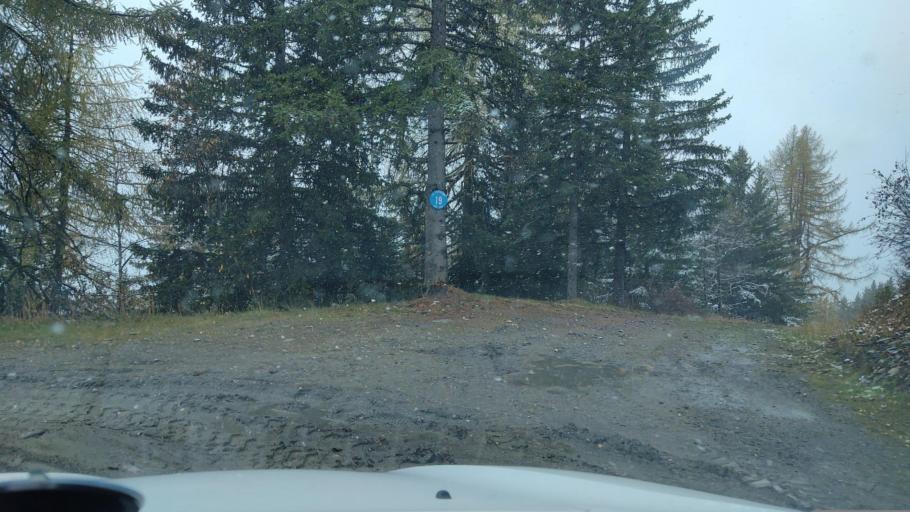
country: FR
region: Rhone-Alpes
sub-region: Departement de la Savoie
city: Seez
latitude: 45.5762
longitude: 6.7921
